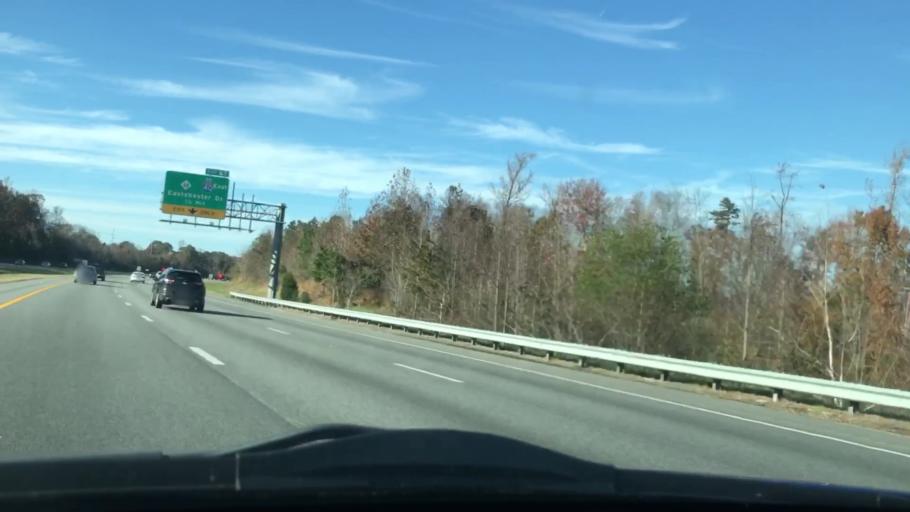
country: US
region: North Carolina
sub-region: Guilford County
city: High Point
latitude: 35.9912
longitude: -79.9828
